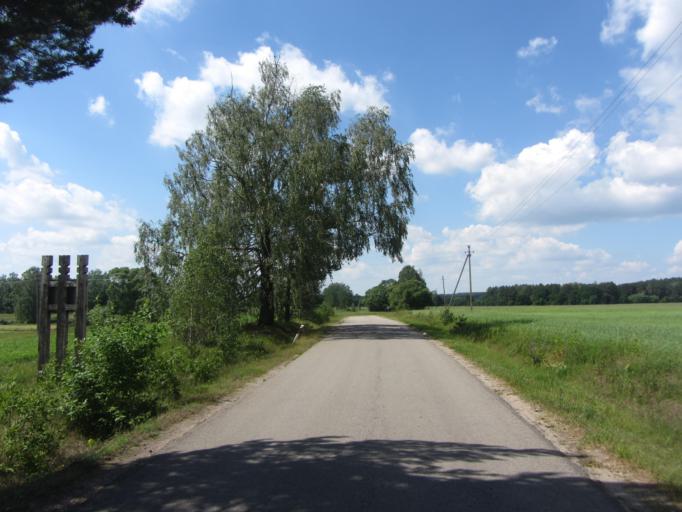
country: LT
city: Birstonas
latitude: 54.5591
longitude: 24.0331
